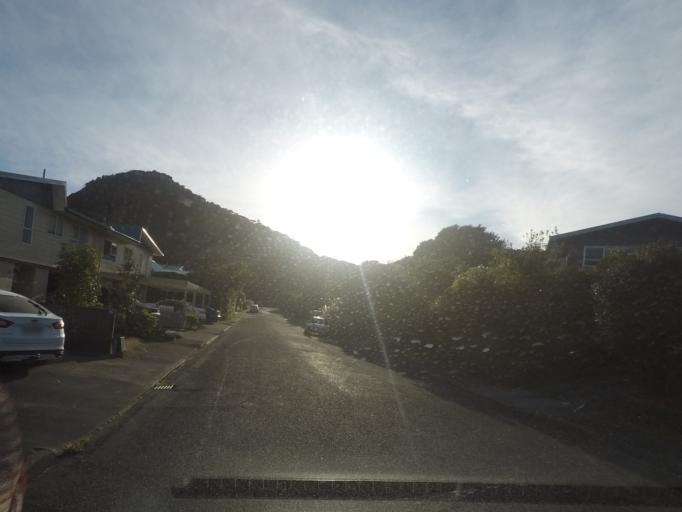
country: NZ
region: Tasman
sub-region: Tasman District
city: Takaka
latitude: -40.8108
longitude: 172.9162
